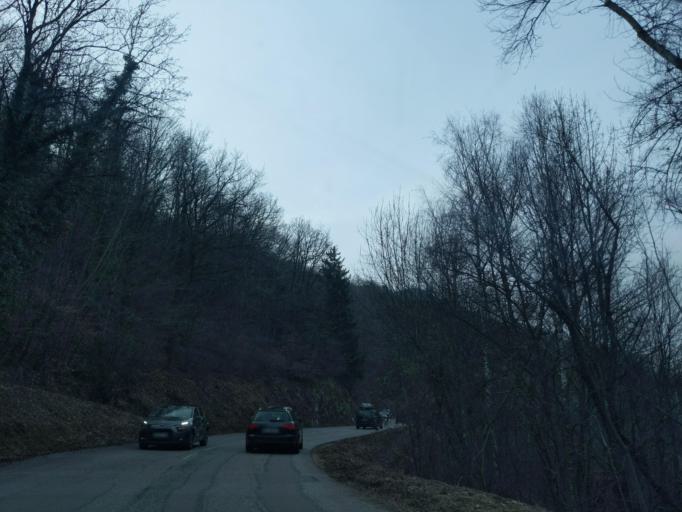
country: FR
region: Rhone-Alpes
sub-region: Departement de la Savoie
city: La Bathie
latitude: 45.6061
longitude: 6.4404
